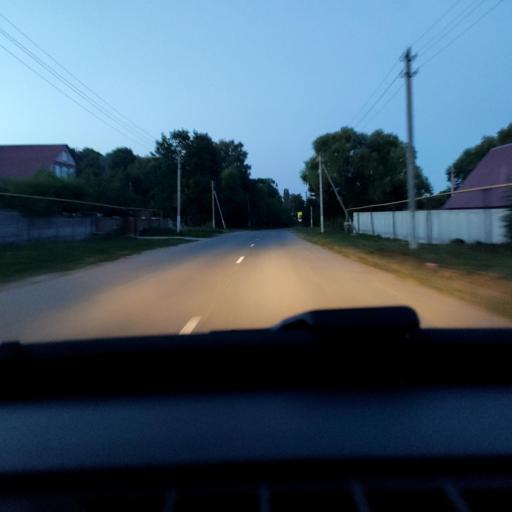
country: RU
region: Lipetsk
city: Zadonsk
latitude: 52.2862
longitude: 38.7477
